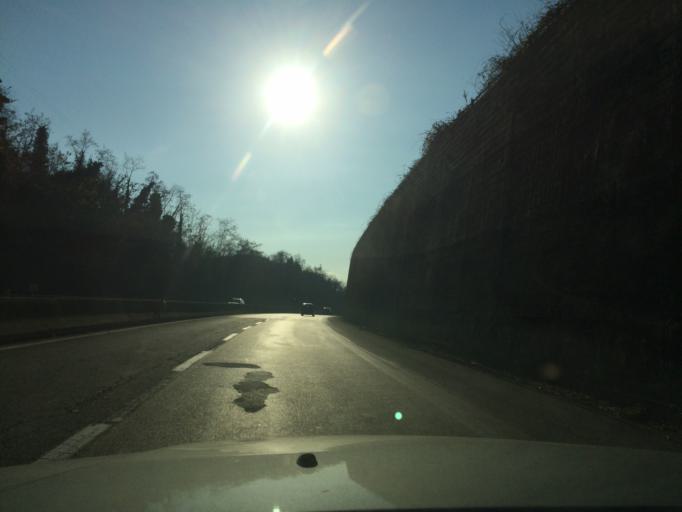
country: IT
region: Umbria
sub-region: Provincia di Terni
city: Fornole
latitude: 42.5348
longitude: 12.4797
